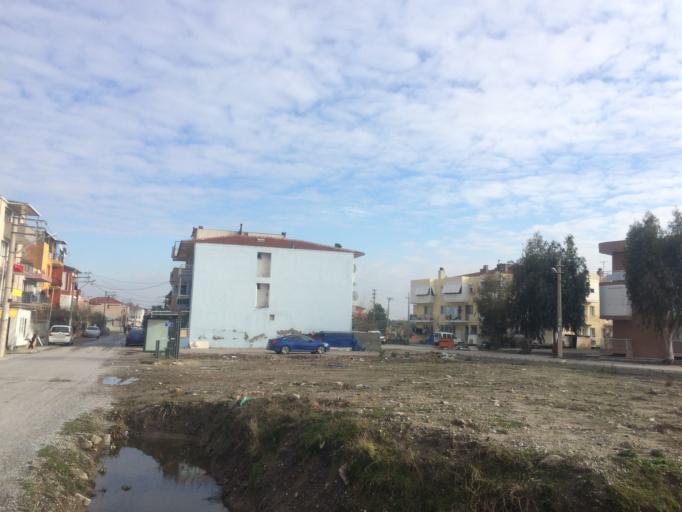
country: TR
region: Izmir
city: Karsiyaka
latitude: 38.4928
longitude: 26.9461
